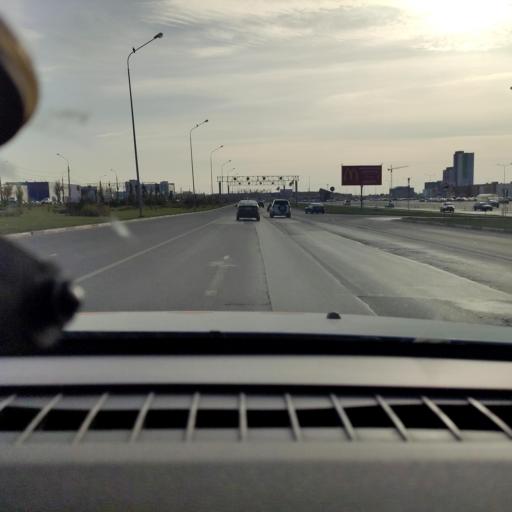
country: RU
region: Samara
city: Samara
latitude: 53.1432
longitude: 50.1775
